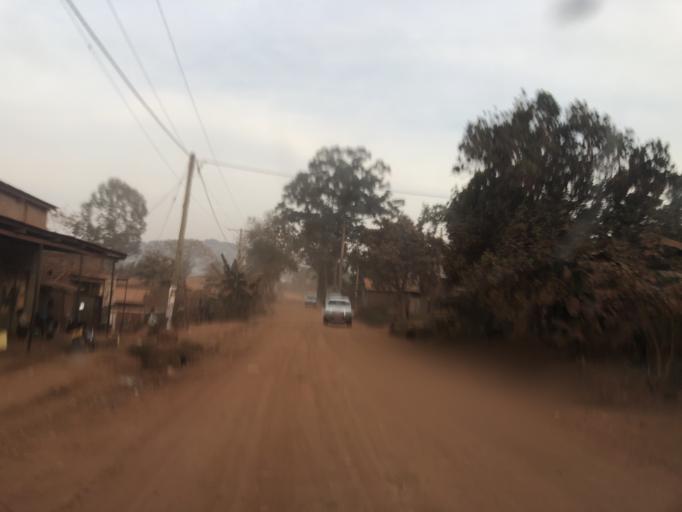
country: UG
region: Central Region
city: Kampala Central Division
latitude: 0.2979
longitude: 32.5187
